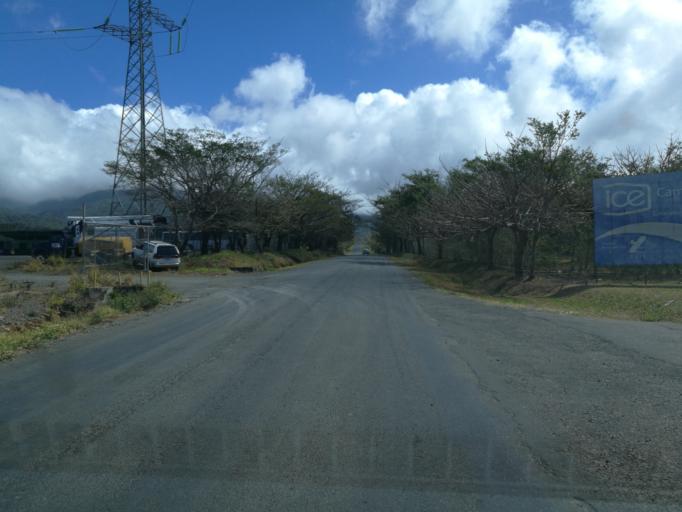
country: CR
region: Guanacaste
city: Liberia
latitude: 10.7591
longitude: -85.3605
